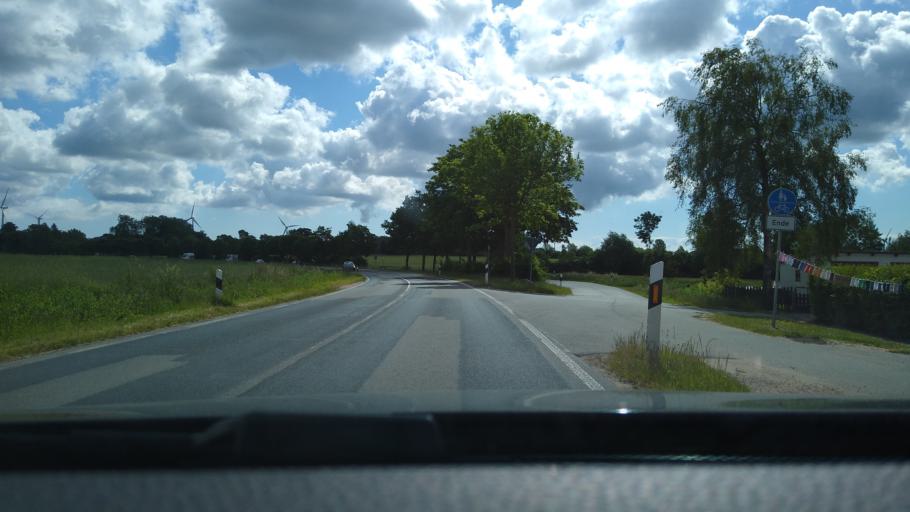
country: DE
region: Schleswig-Holstein
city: Kabelhorst
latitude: 54.2118
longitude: 10.9300
